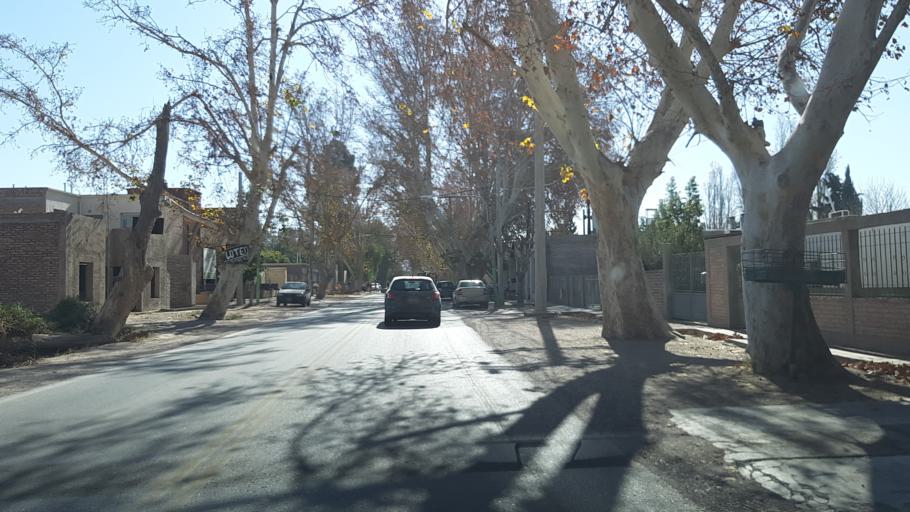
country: AR
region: San Juan
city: San Juan
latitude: -31.5260
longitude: -68.5953
